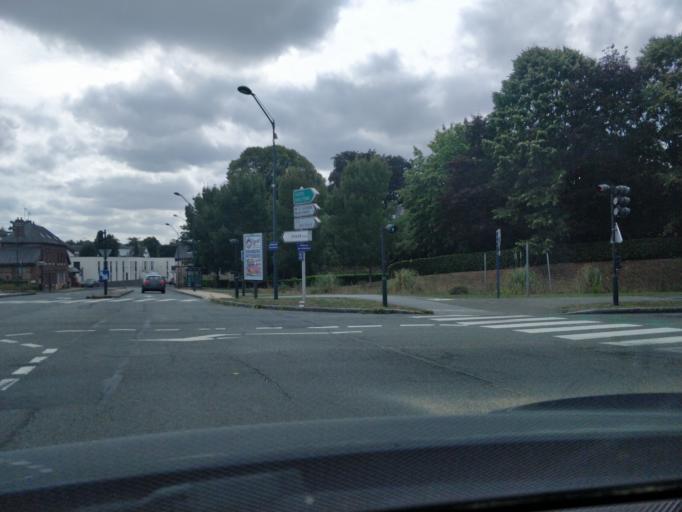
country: FR
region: Haute-Normandie
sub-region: Departement de la Seine-Maritime
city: Bois-Guillaume
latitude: 49.4727
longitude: 1.1124
